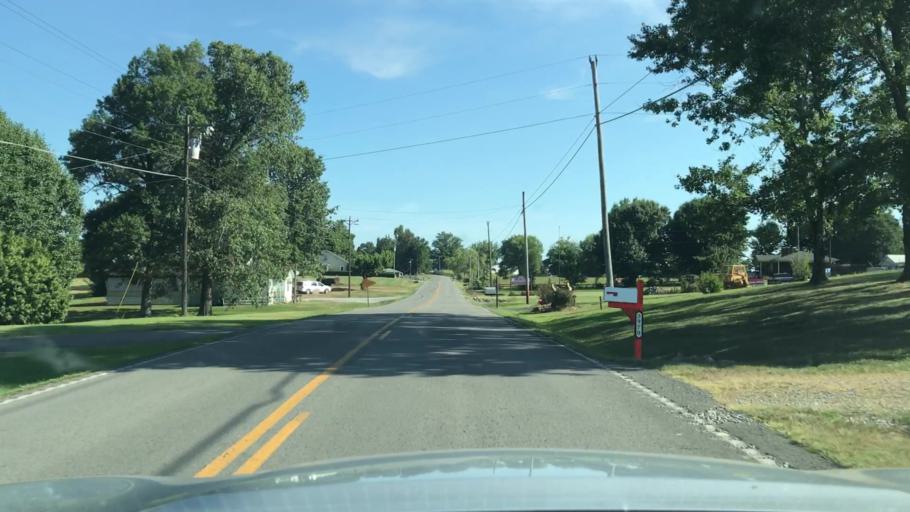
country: US
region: Kentucky
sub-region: Muhlenberg County
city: Greenville
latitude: 37.1564
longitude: -87.1419
